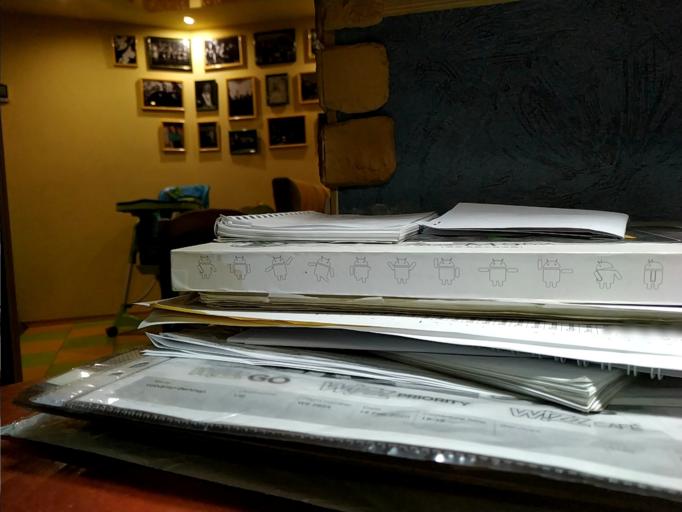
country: RU
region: Arkhangelskaya
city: Konevo
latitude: 62.2611
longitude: 38.8752
